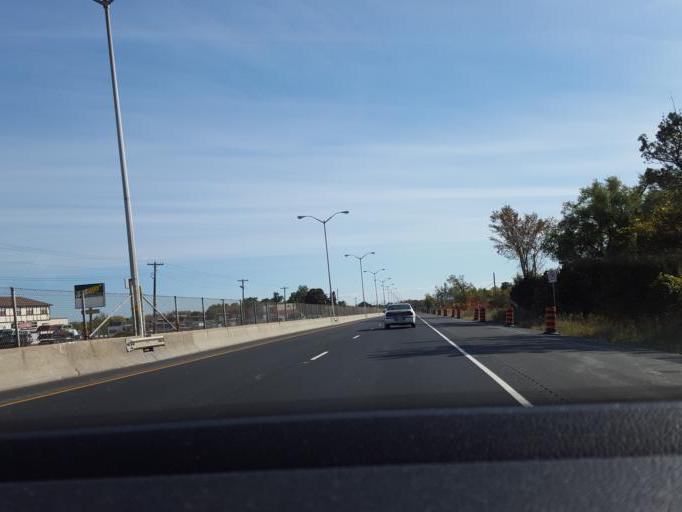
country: CA
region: Ontario
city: Oshawa
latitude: 43.9412
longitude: -78.6027
